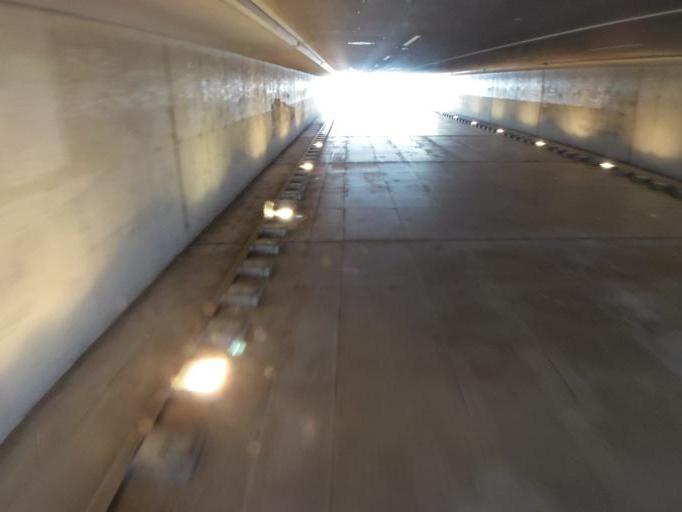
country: DE
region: Saxony
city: Leipzig
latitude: 51.3452
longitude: 12.3513
